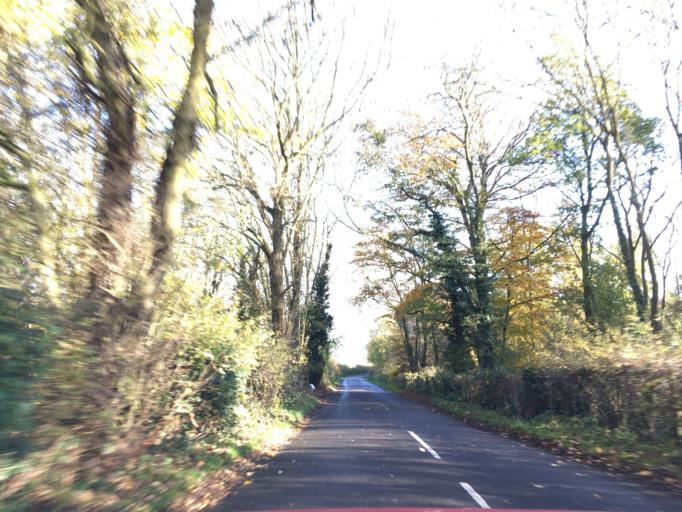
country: GB
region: England
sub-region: Warwickshire
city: Alcester
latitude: 52.1875
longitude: -1.8912
